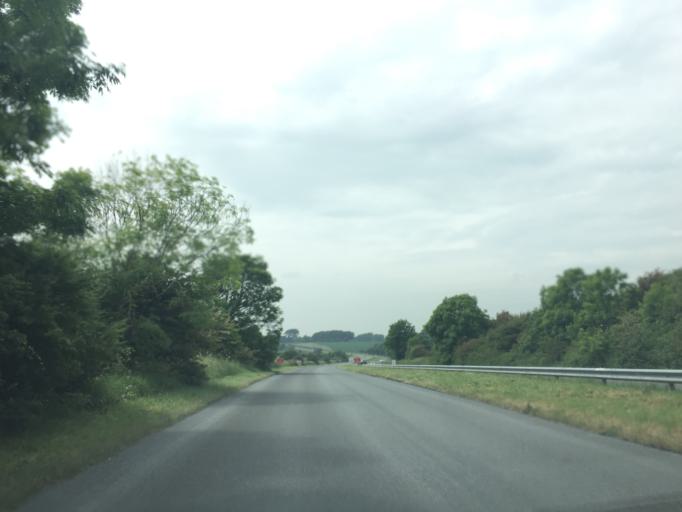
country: GB
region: England
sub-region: Dorset
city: Overcombe
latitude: 50.6647
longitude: -2.3424
